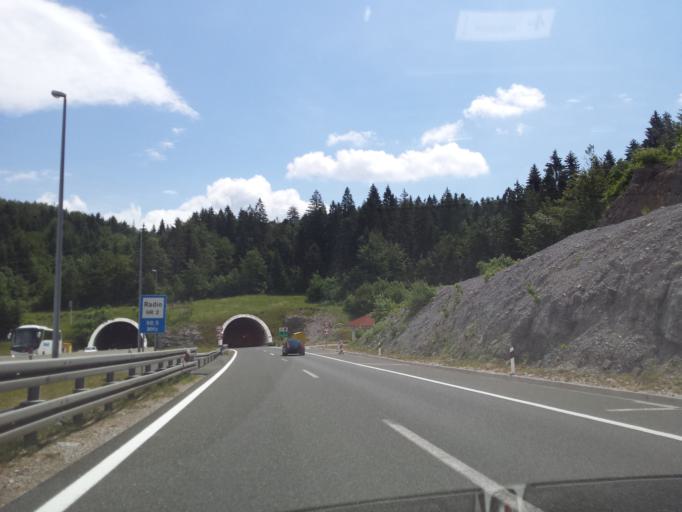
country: HR
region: Primorsko-Goranska
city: Vrbovsko
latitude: 45.3734
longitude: 15.0058
